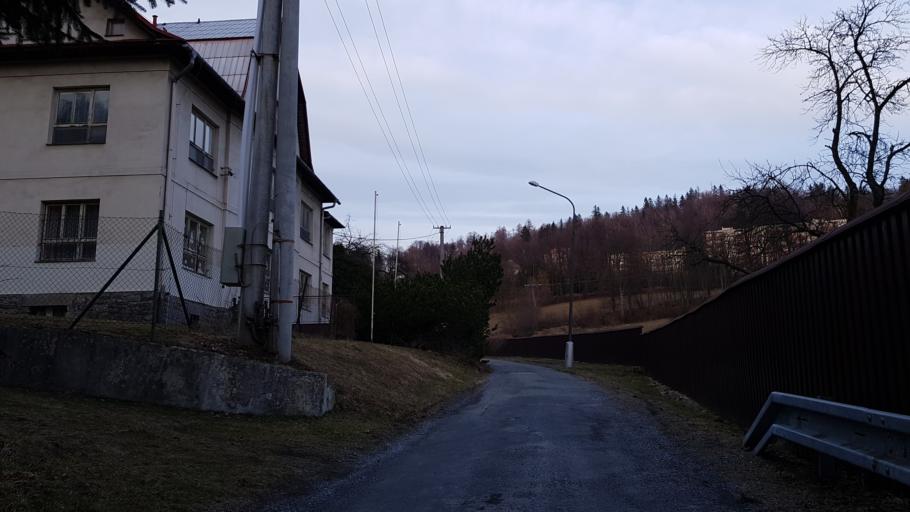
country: CZ
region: Olomoucky
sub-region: Okres Jesenik
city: Jesenik
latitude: 50.2347
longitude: 17.1855
